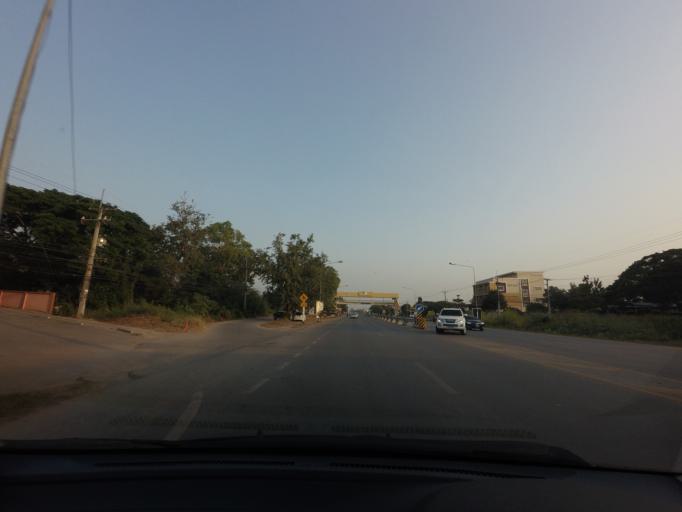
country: TH
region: Sukhothai
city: Sukhothai
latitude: 17.0160
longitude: 99.8323
